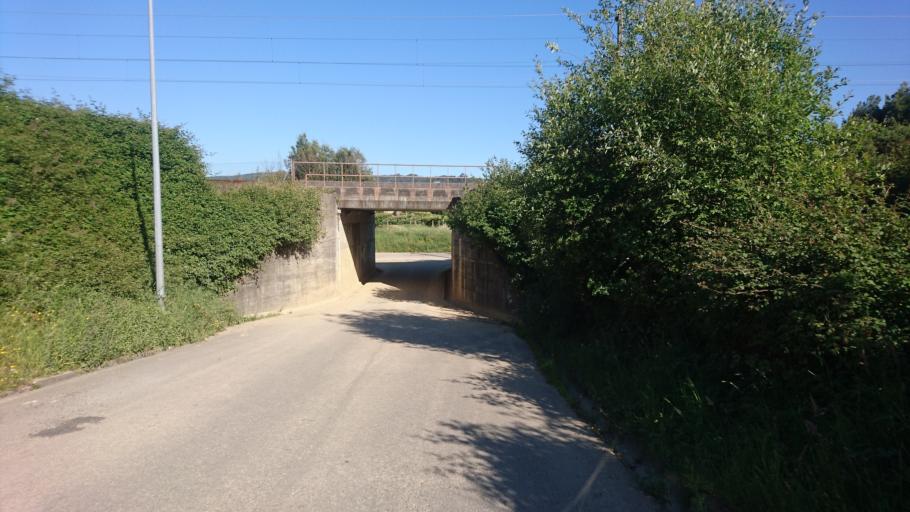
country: PT
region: Porto
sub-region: Paredes
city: Recarei
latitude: 41.1535
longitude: -8.3855
